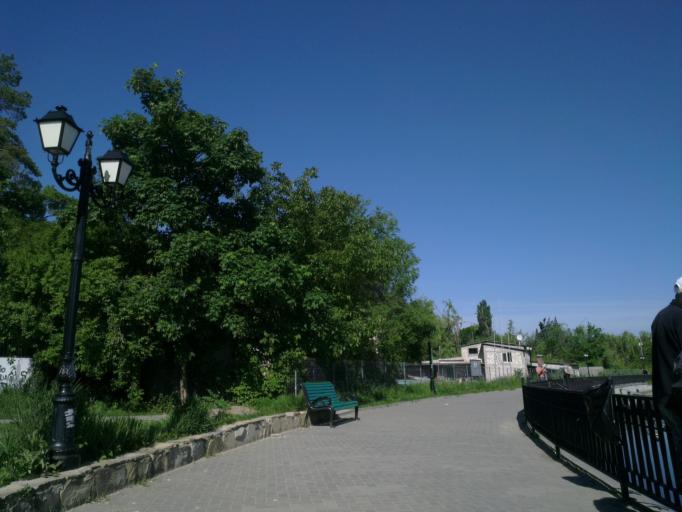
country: MD
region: Chisinau
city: Chisinau
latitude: 47.0154
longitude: 28.8088
